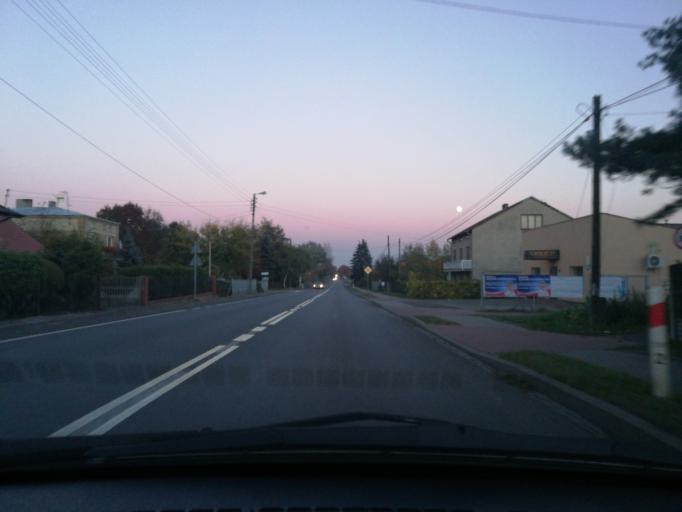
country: PL
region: Lodz Voivodeship
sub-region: Powiat brzezinski
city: Brzeziny
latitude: 51.8062
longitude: 19.6724
